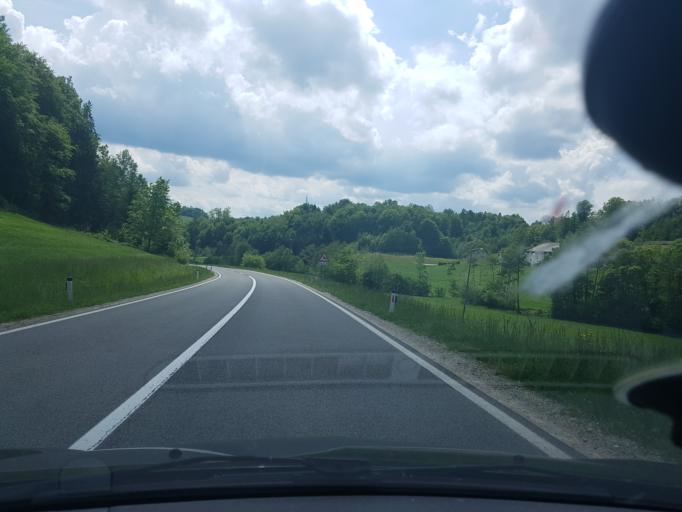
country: SI
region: Rogaska Slatina
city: Rogaska Slatina
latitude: 46.2491
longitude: 15.6044
